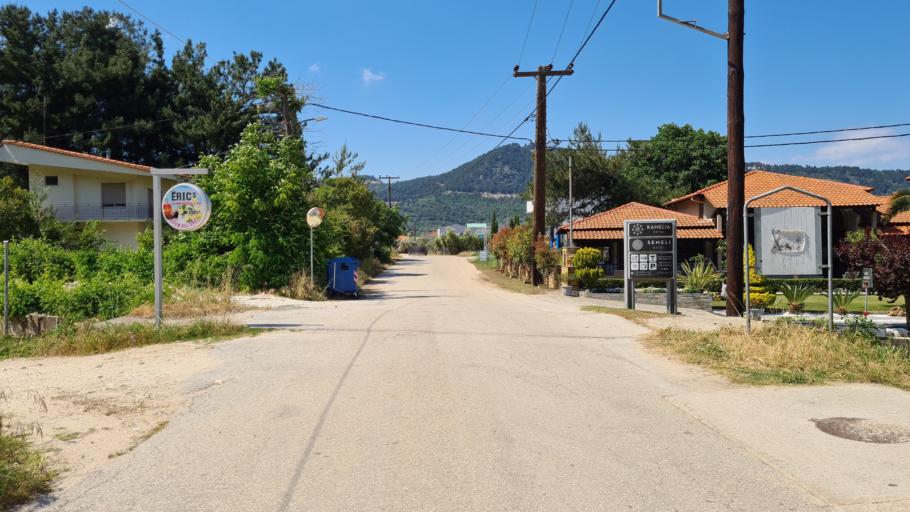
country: GR
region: East Macedonia and Thrace
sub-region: Nomos Kavalas
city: Potamia
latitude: 40.7105
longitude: 24.7581
